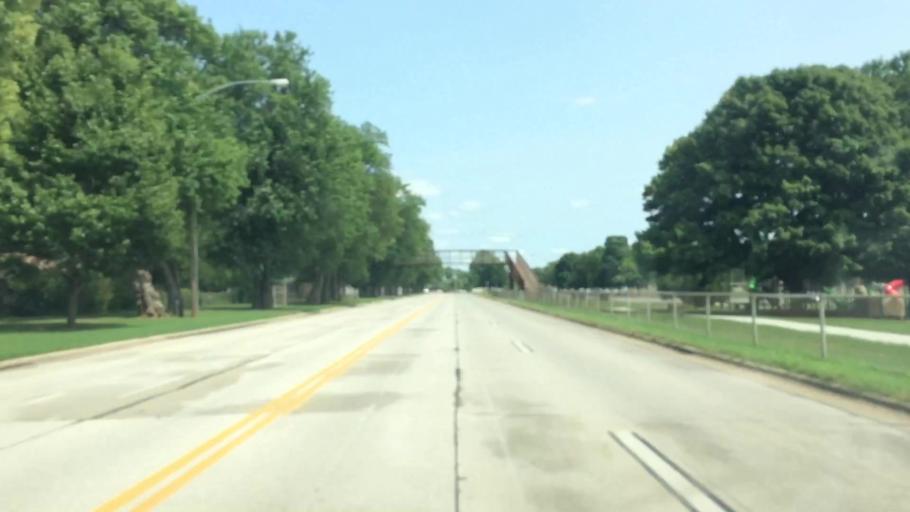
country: US
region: Missouri
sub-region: Greene County
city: Springfield
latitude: 37.1670
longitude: -93.2698
